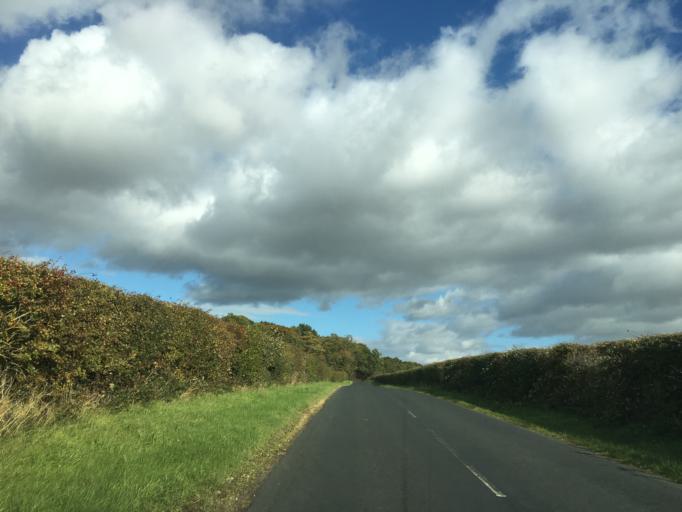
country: GB
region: Scotland
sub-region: East Lothian
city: Pencaitland
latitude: 55.8916
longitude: -2.9104
